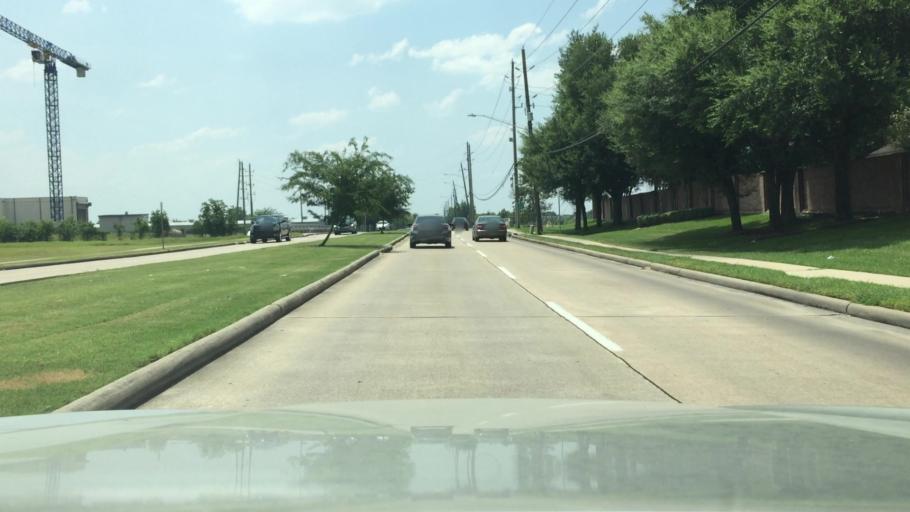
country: US
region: Texas
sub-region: Fort Bend County
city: Meadows Place
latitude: 29.7237
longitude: -95.5924
